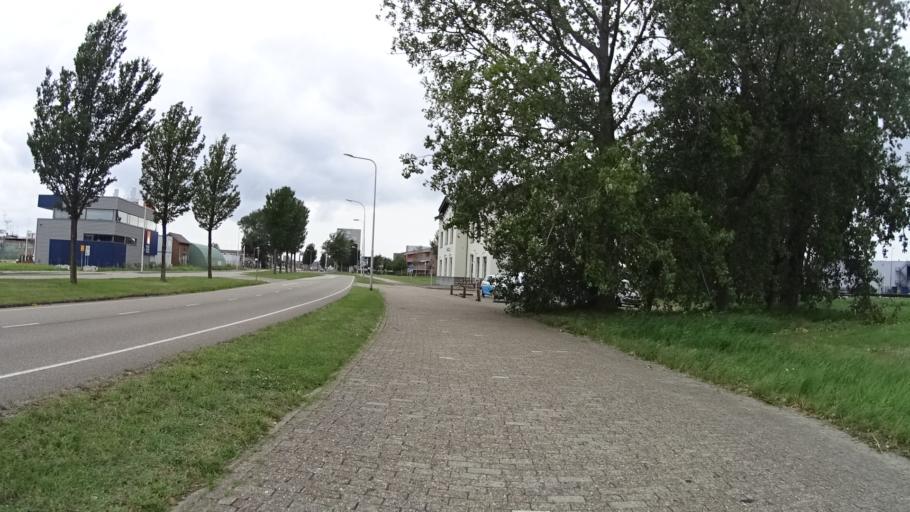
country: NL
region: Zeeland
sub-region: Gemeente Vlissingen
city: Vlissingen
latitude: 51.4480
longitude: 3.5935
